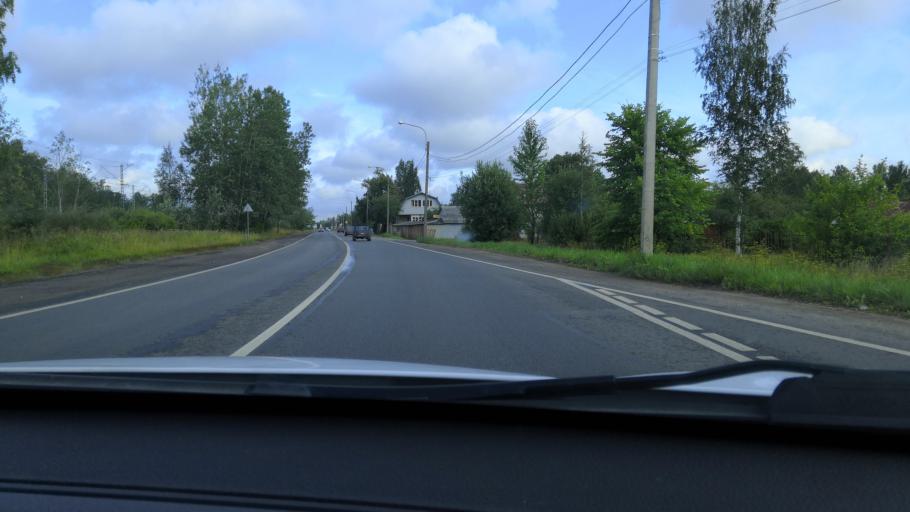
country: RU
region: St.-Petersburg
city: Tyarlevo
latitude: 59.7055
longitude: 30.4387
